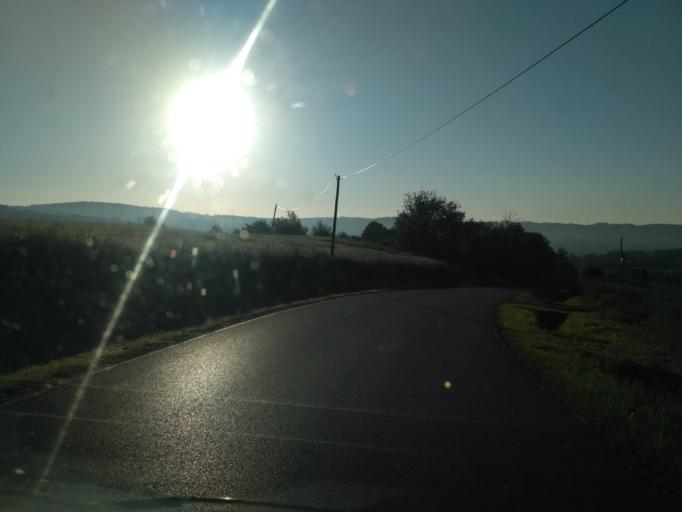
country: PL
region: Subcarpathian Voivodeship
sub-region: Powiat strzyzowski
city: Polomia
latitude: 49.8974
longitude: 21.8683
